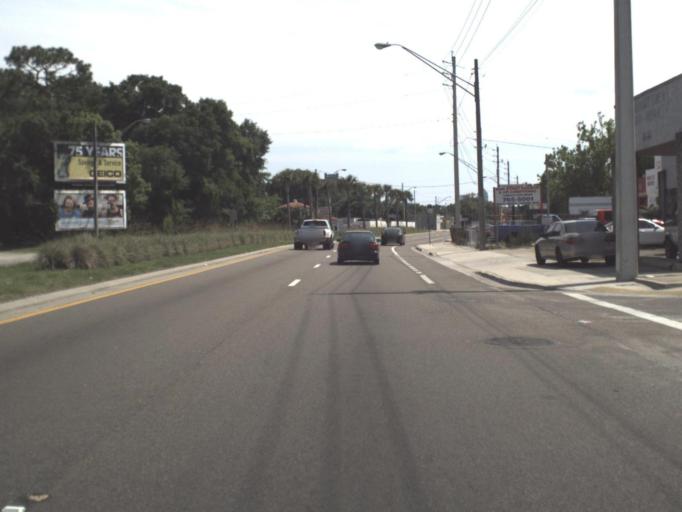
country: US
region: Florida
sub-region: Duval County
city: Jacksonville
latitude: 30.3720
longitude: -81.6515
